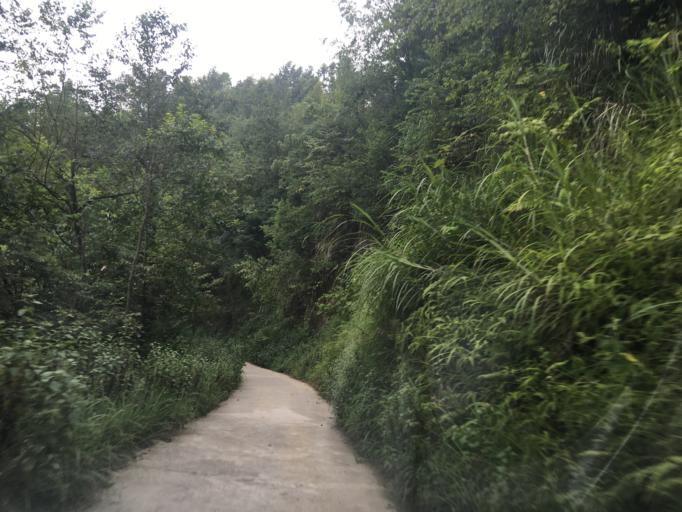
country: CN
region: Guangxi Zhuangzu Zizhiqu
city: Xinzhou
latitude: 25.1589
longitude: 105.6988
